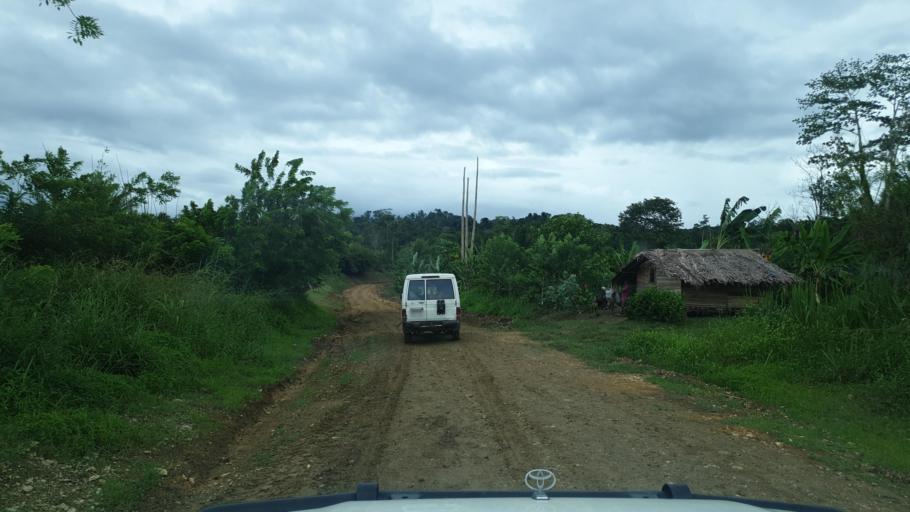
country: PG
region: Gulf
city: Kerema
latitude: -7.9888
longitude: 145.8311
